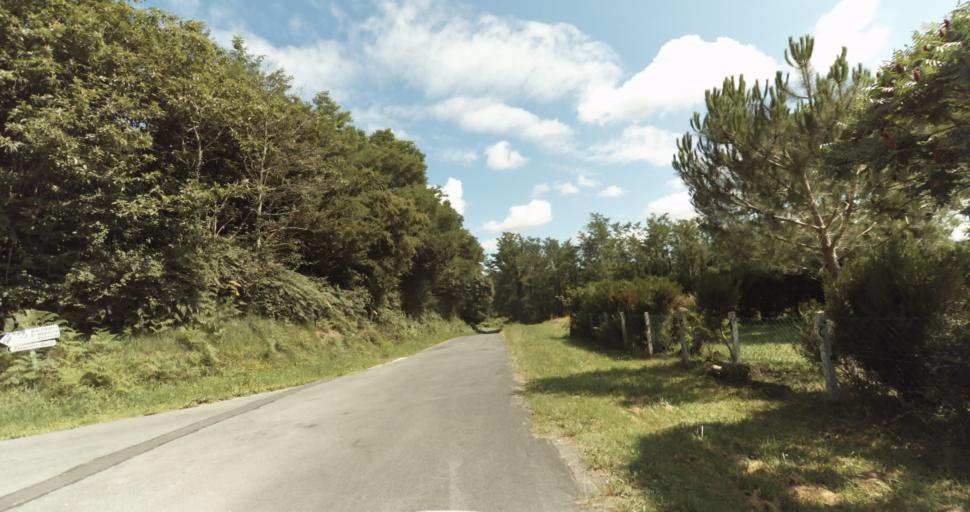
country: FR
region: Aquitaine
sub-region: Departement de la Gironde
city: Bazas
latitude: 44.4631
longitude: -0.2180
